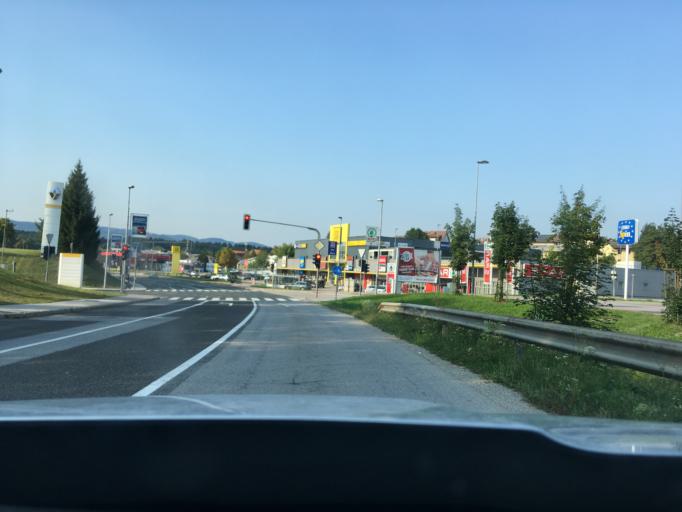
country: SI
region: Novo Mesto
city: Novo Mesto
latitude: 45.7954
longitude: 15.1807
